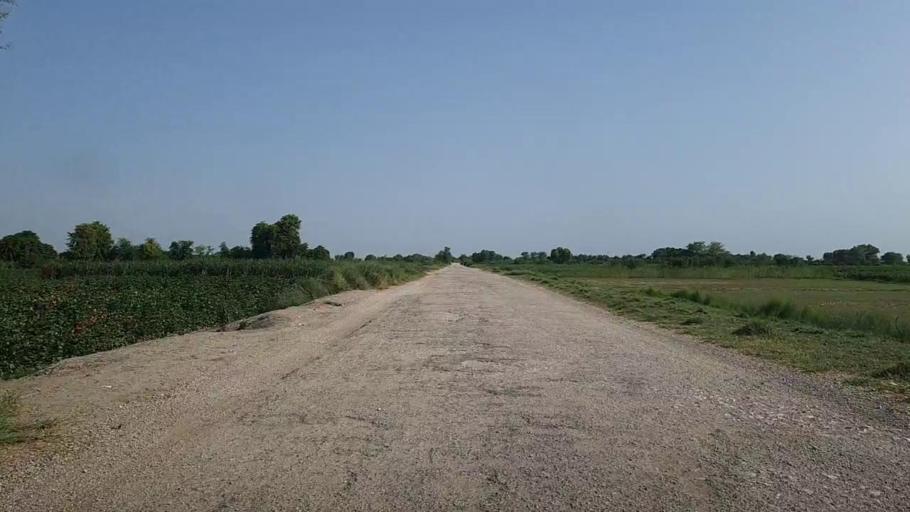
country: PK
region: Sindh
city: Karaundi
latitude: 26.8749
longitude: 68.3281
